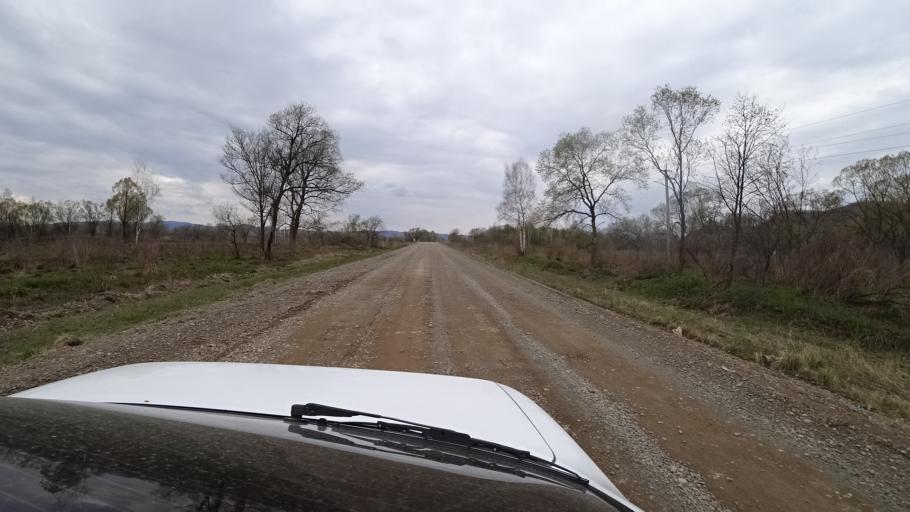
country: RU
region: Primorskiy
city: Novopokrovka
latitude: 45.5619
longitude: 134.3357
